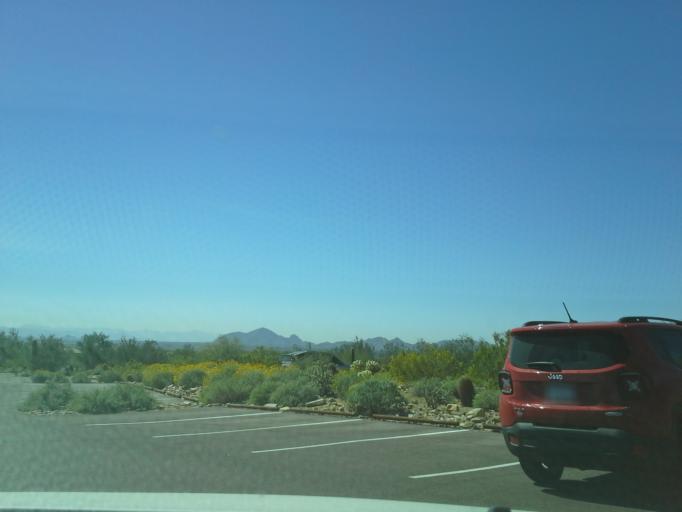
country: US
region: Arizona
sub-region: Maricopa County
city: Fountain Hills
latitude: 33.5995
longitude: -111.8126
